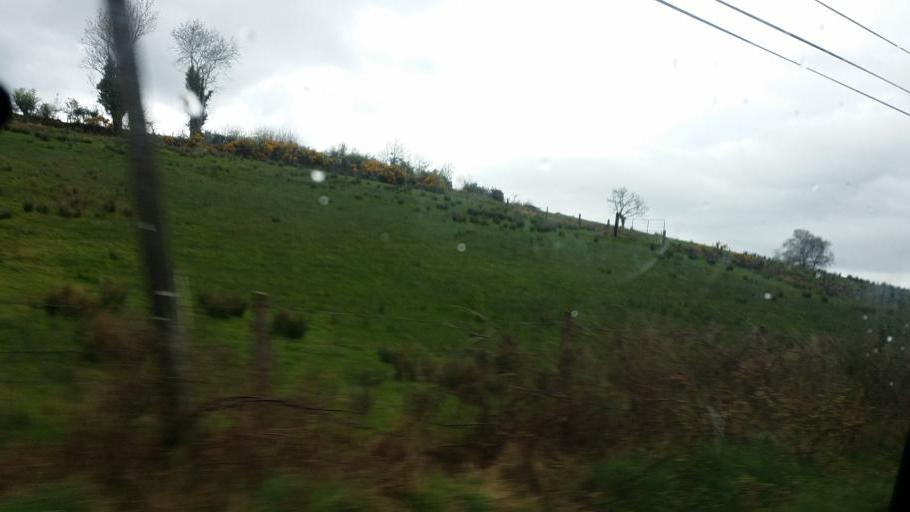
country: IE
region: Ulster
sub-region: An Cabhan
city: Ballyconnell
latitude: 54.1146
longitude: -7.6191
